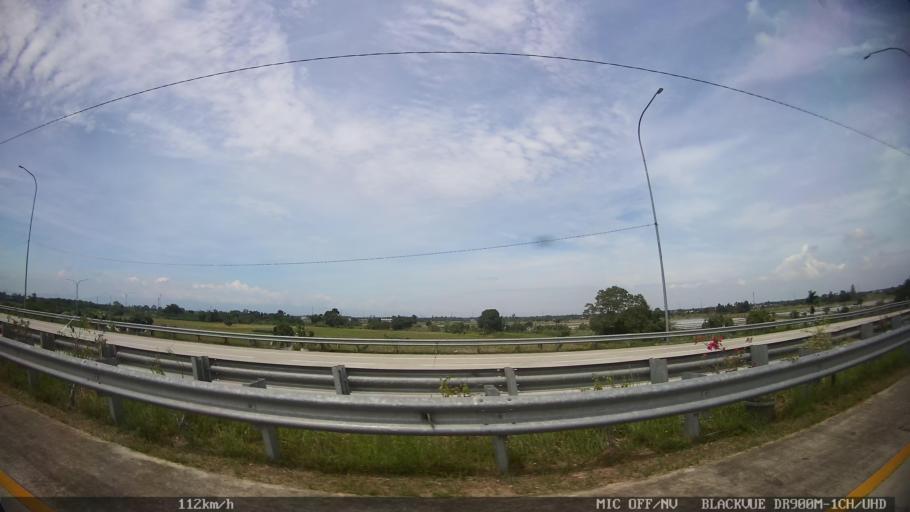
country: ID
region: North Sumatra
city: Percut
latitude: 3.5637
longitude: 98.8497
